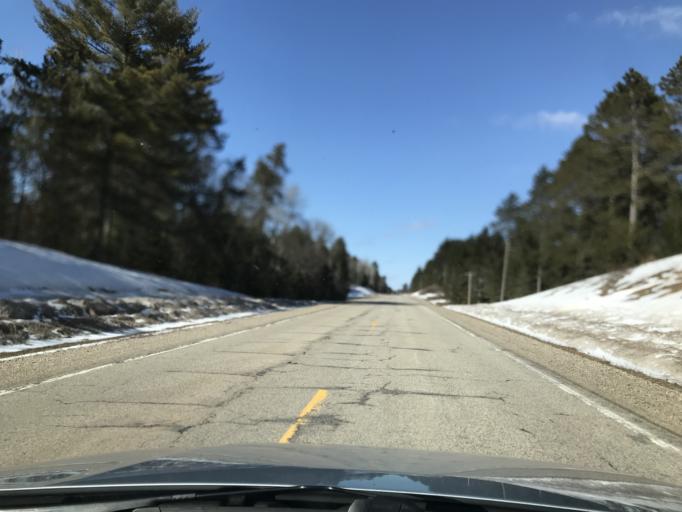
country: US
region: Wisconsin
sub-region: Marinette County
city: Niagara
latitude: 45.3910
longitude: -88.0995
